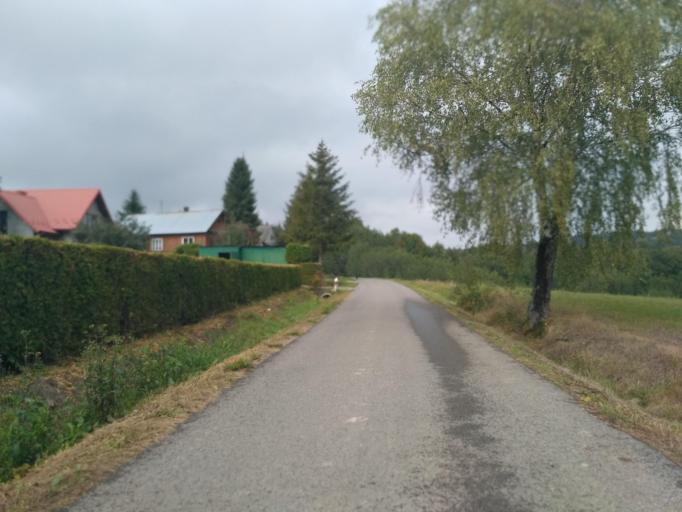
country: PL
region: Subcarpathian Voivodeship
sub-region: Powiat debicki
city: Brzostek
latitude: 49.9433
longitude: 21.4503
